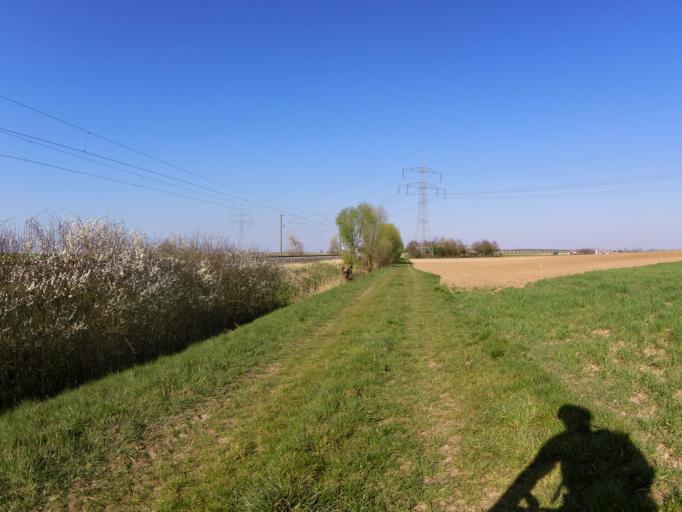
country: DE
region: Bavaria
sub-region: Regierungsbezirk Unterfranken
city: Oberpleichfeld
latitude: 49.8301
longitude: 10.0855
